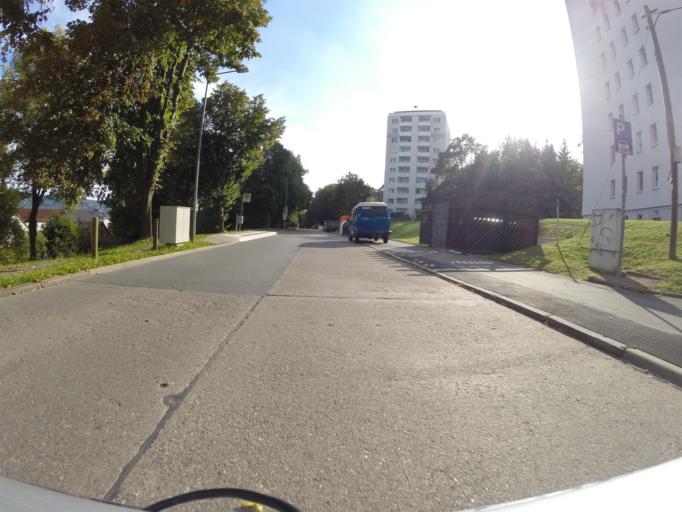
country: DE
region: Thuringia
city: Jena
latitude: 50.9509
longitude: 11.5972
